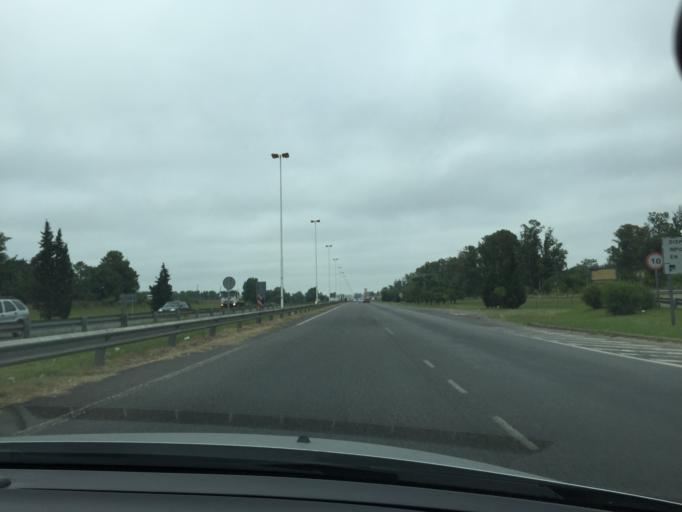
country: AR
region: Buenos Aires
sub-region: Partido de Ezeiza
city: Ezeiza
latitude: -34.8557
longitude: -58.5549
